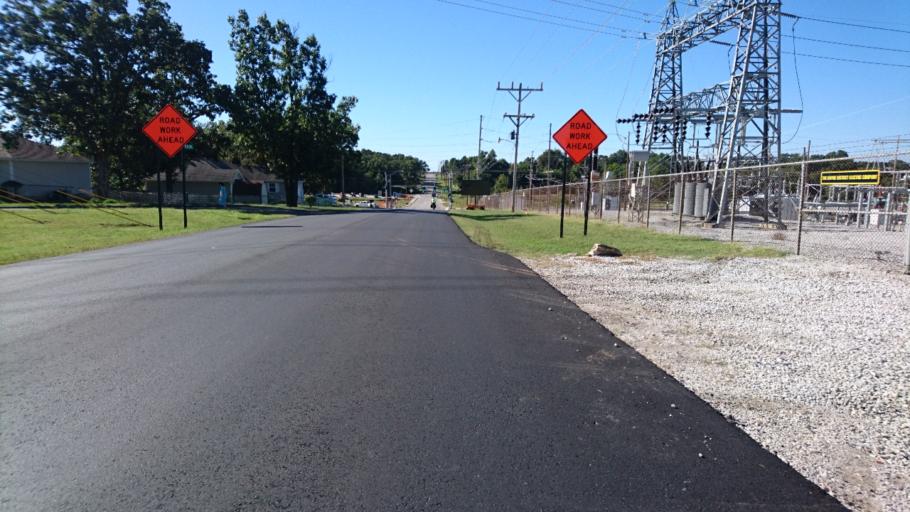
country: US
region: Missouri
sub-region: Jasper County
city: Joplin
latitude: 37.1145
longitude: -94.4940
